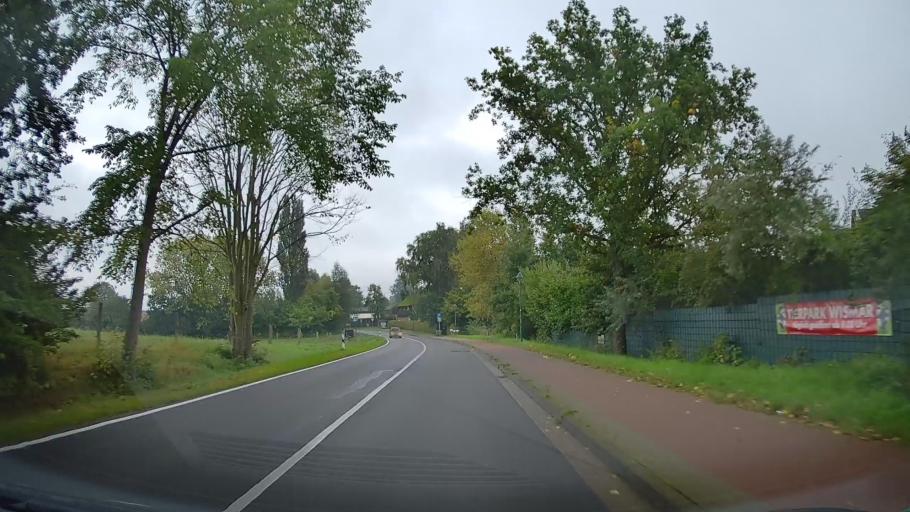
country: DE
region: Mecklenburg-Vorpommern
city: Ostseebad Boltenhagen
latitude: 53.9415
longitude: 11.2395
